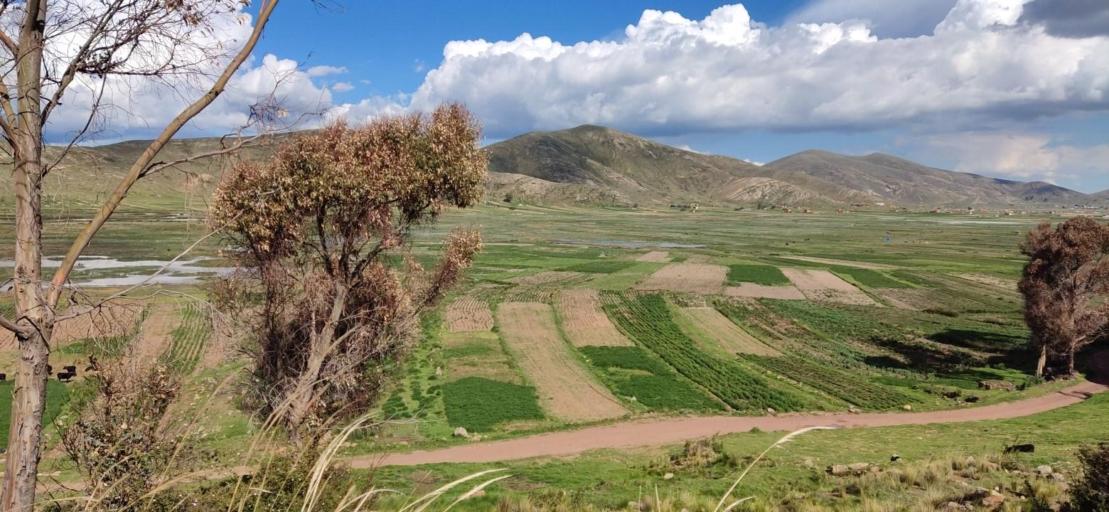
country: BO
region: La Paz
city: Batallas
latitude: -16.3418
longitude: -68.6361
